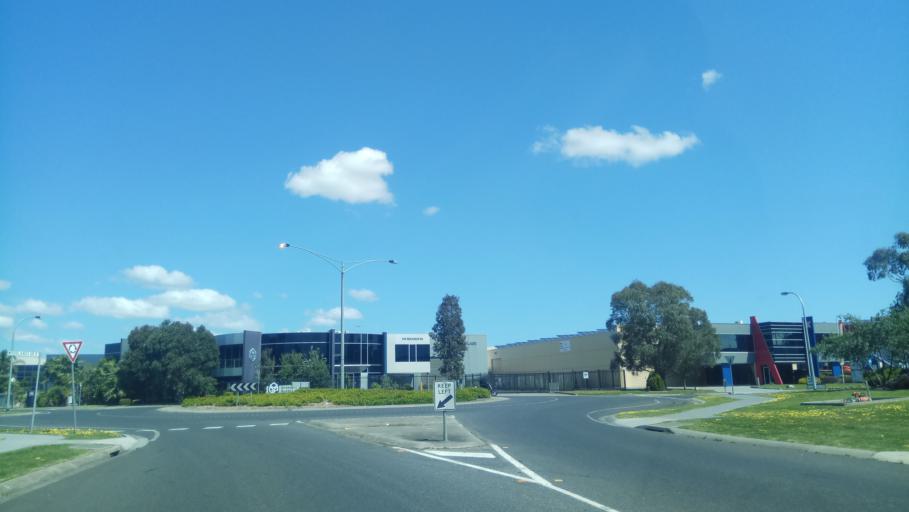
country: AU
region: Victoria
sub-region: Kingston
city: Waterways
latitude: -38.0007
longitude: 145.1186
